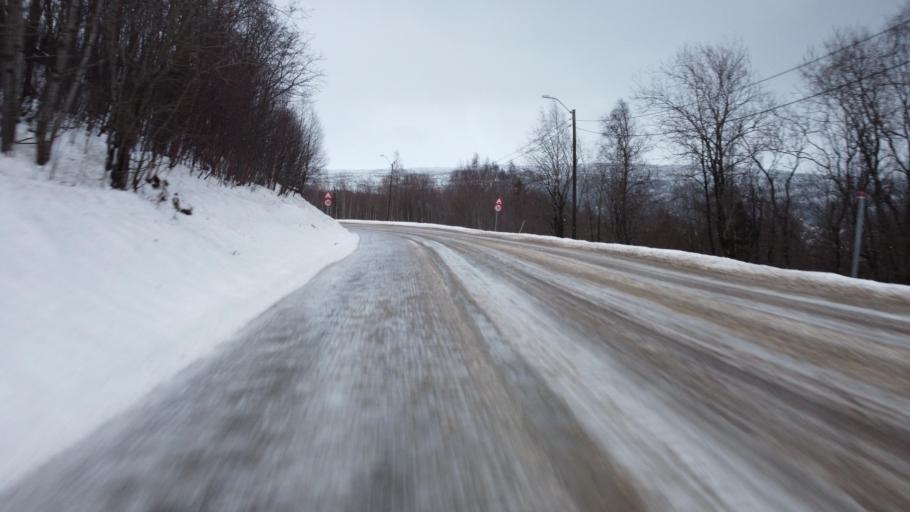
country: NO
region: Nordland
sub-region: Rana
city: Mo i Rana
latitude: 66.3280
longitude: 14.1540
